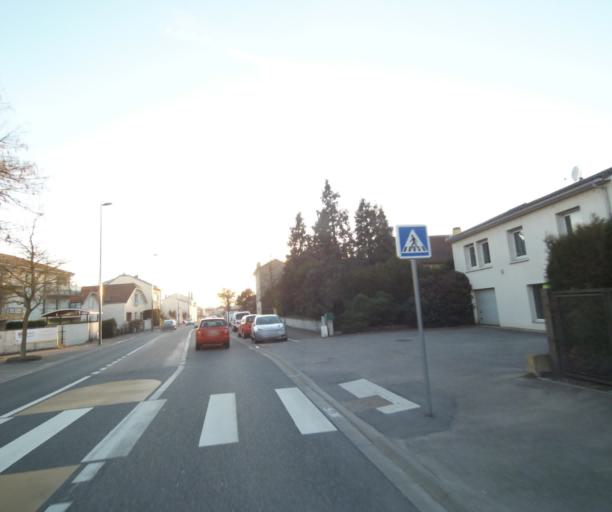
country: FR
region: Lorraine
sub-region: Departement de Meurthe-et-Moselle
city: Essey-les-Nancy
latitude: 48.7068
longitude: 6.2335
